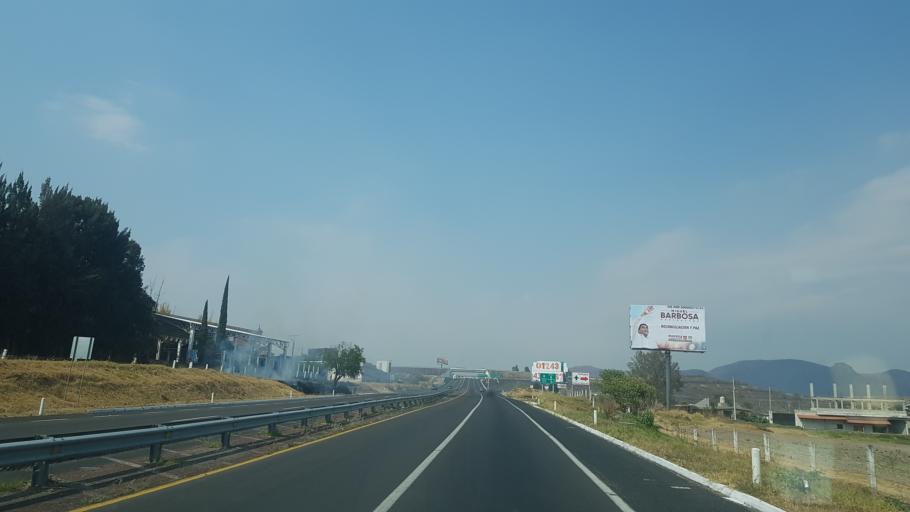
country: MX
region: Puebla
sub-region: Atlixco
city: San Agustin Huixaxtla
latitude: 18.9321
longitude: -98.3948
